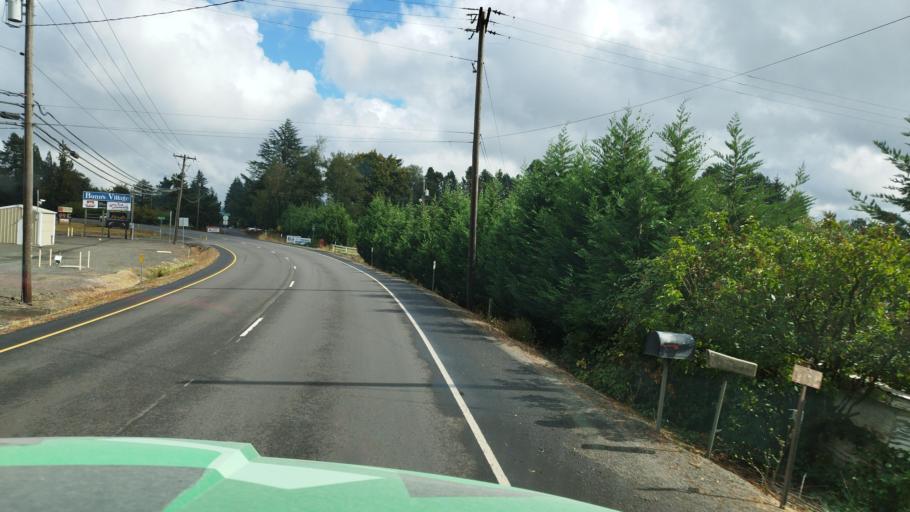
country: US
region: Oregon
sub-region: Yamhill County
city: Lafayette
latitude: 45.2338
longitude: -123.1534
